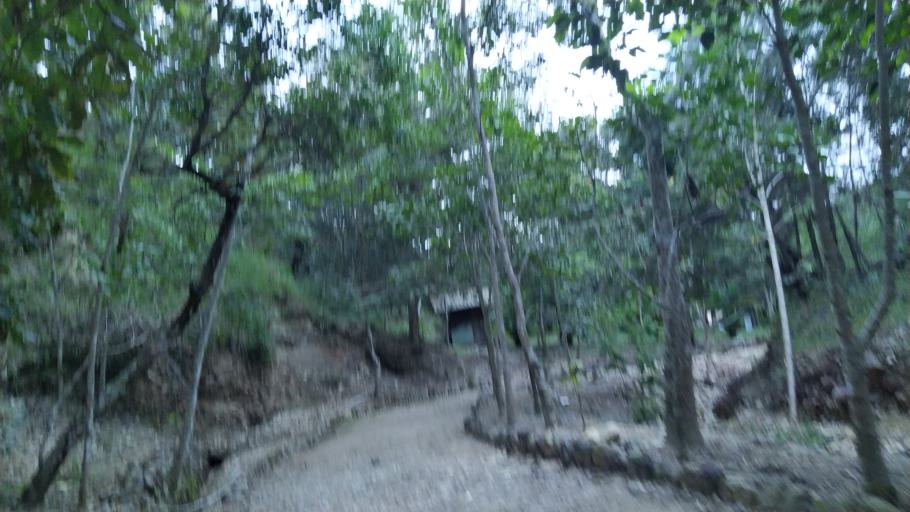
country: GT
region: Chiquimula
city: Esquipulas
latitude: 14.5575
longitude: -89.3173
